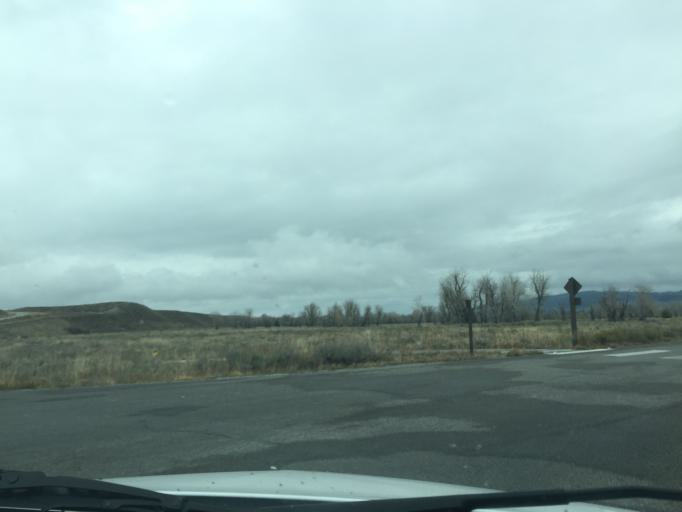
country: US
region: Wyoming
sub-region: Teton County
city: Moose Wilson Road
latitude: 43.6634
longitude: -110.7223
